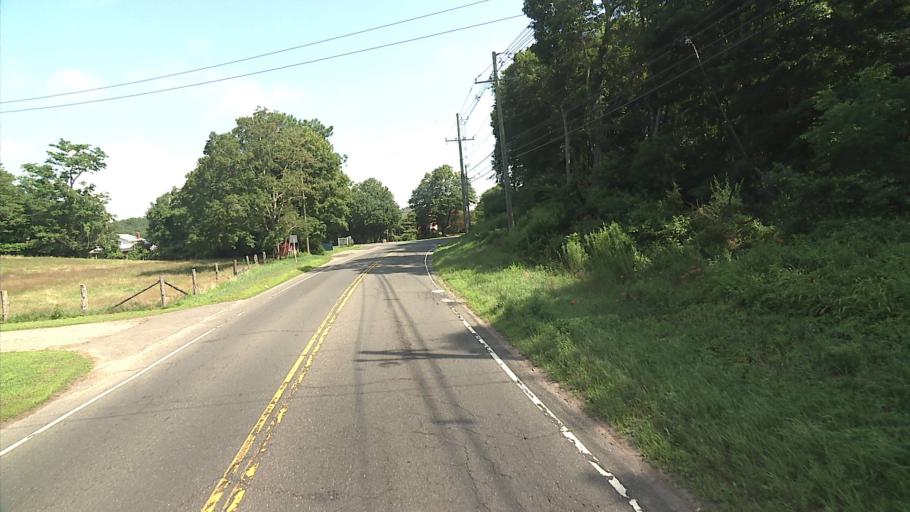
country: US
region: Connecticut
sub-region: Middlesex County
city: Westbrook Center
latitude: 41.2999
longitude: -72.4396
